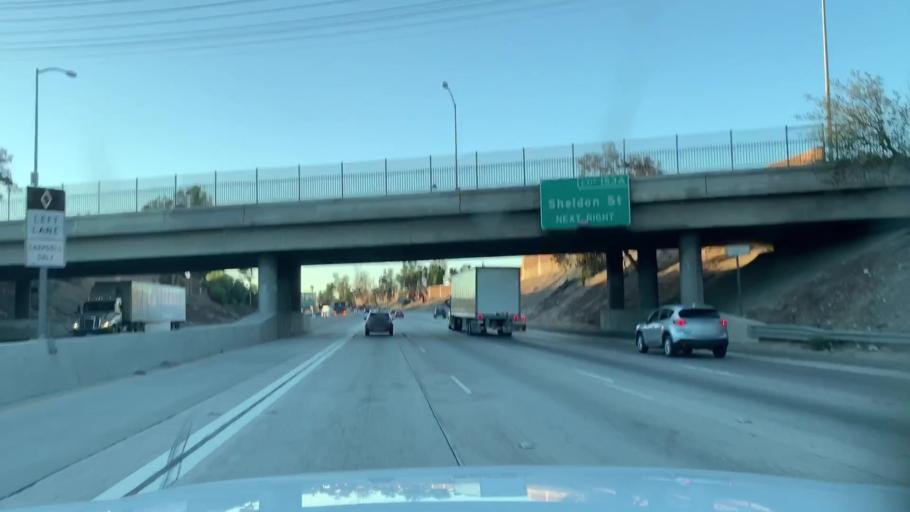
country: US
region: California
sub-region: Los Angeles County
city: North Hollywood
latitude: 34.2288
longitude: -118.3927
